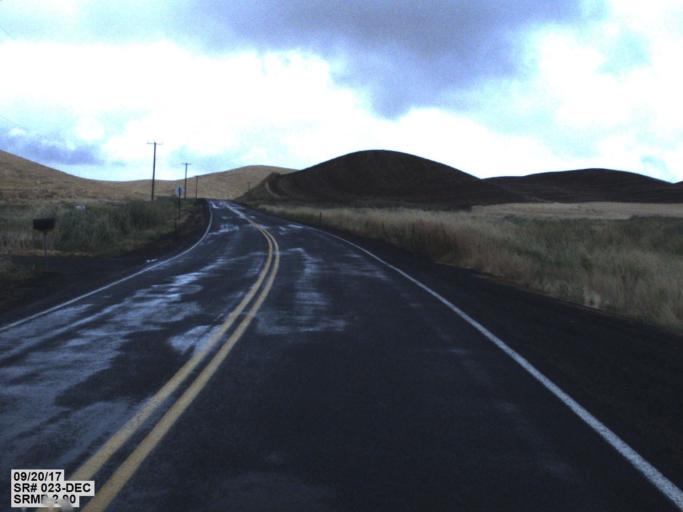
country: US
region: Washington
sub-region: Whitman County
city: Colfax
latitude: 47.0011
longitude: -117.4127
